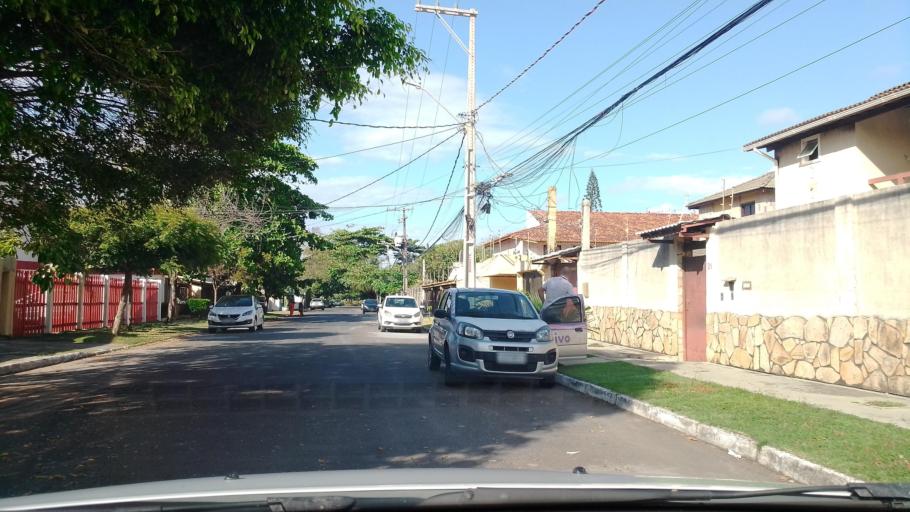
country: BR
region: Bahia
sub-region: Lauro De Freitas
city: Lauro de Freitas
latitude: -12.9403
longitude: -38.3335
